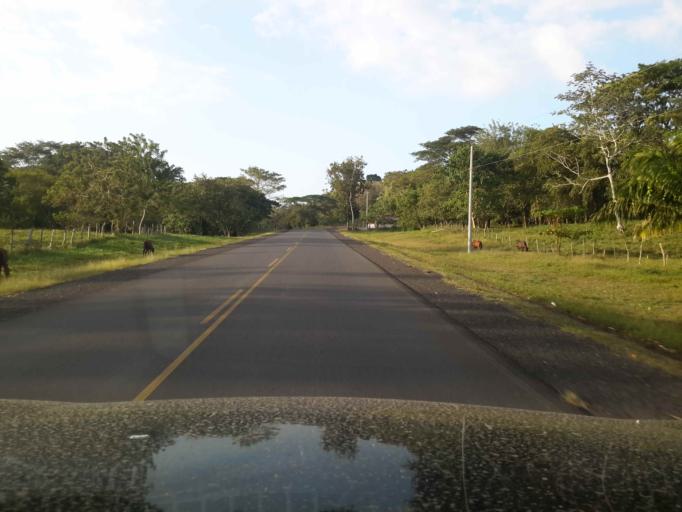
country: NI
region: Rio San Juan
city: San Miguelito
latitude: 11.3605
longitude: -84.7643
